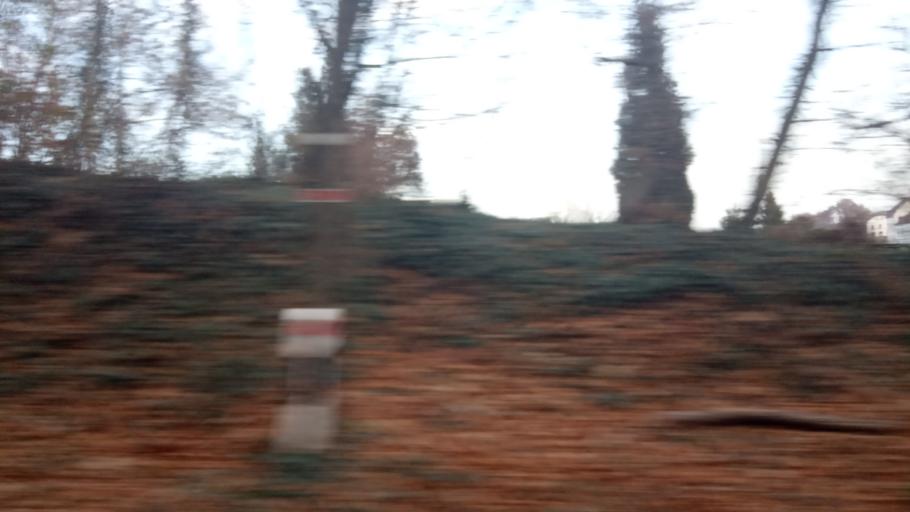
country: DE
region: North Rhine-Westphalia
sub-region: Regierungsbezirk Dusseldorf
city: Velbert
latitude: 51.3812
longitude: 7.0612
